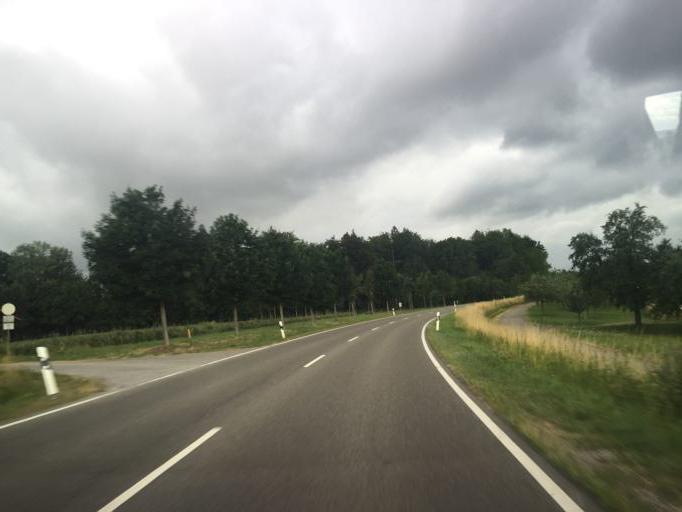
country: DE
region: Baden-Wuerttemberg
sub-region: Regierungsbezirk Stuttgart
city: Nufringen
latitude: 48.6442
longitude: 8.8686
